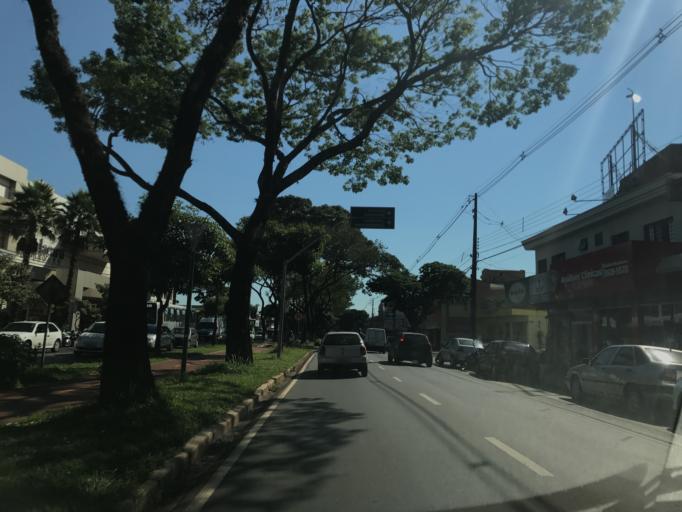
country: BR
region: Parana
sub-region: Maringa
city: Maringa
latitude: -23.4139
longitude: -51.9550
